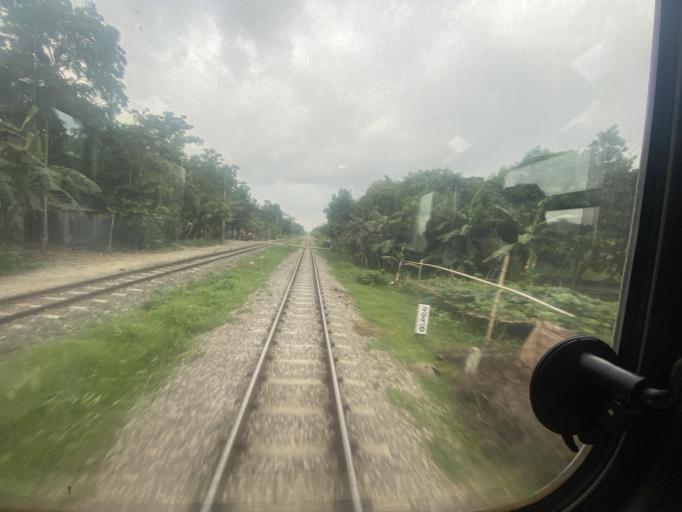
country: BD
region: Dhaka
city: Narsingdi
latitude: 23.9308
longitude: 90.6919
